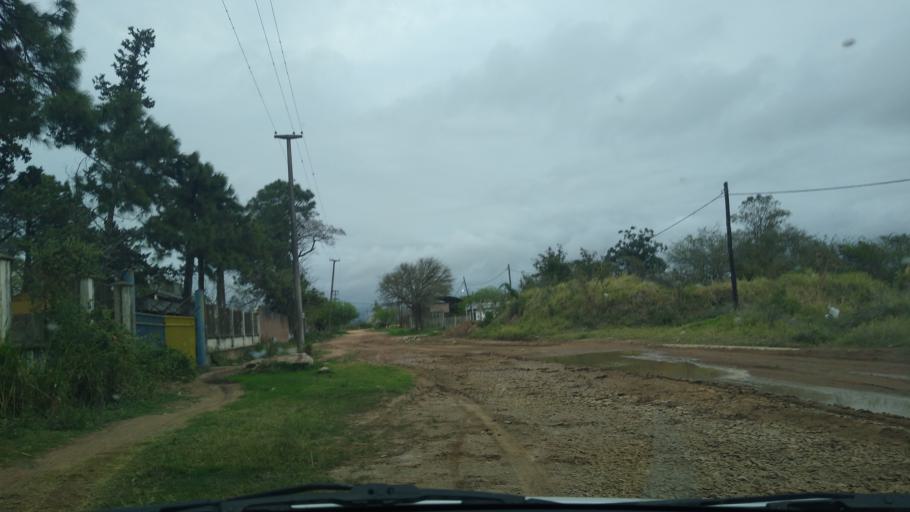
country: AR
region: Chaco
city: Barranqueras
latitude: -27.4737
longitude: -58.9117
